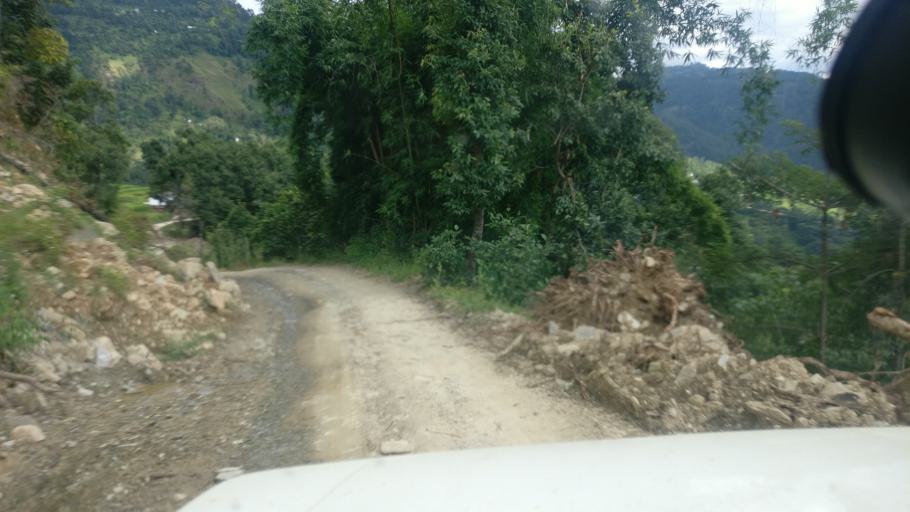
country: NP
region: Western Region
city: Baglung
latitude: 28.2604
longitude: 83.6515
